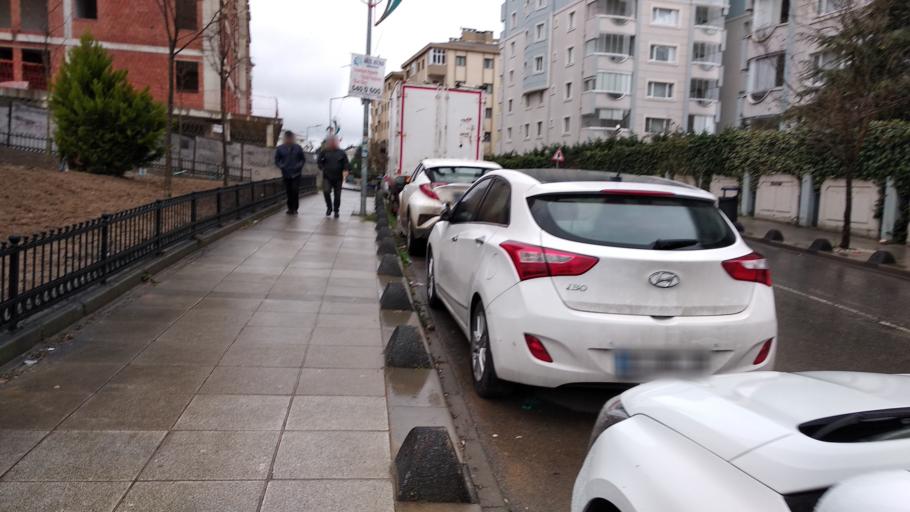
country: TR
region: Istanbul
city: Samandira
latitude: 41.0219
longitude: 29.1870
